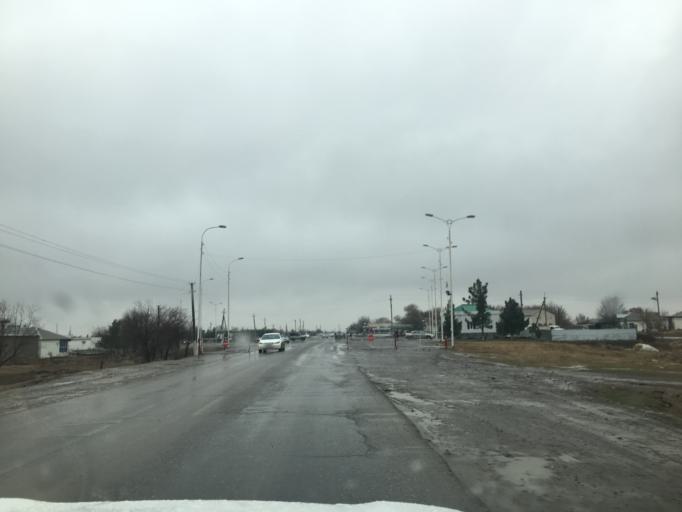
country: TM
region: Mary
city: Yoloeten
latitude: 37.2879
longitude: 62.3499
